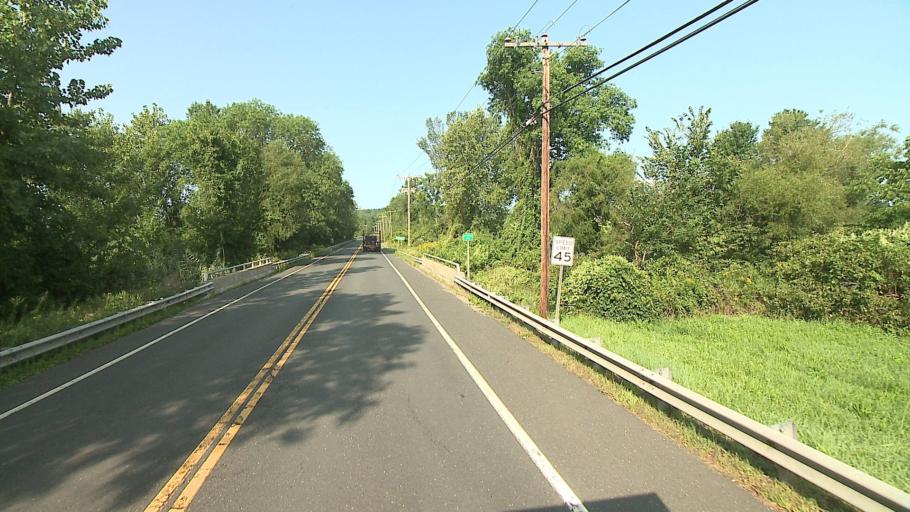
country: US
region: Connecticut
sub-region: Litchfield County
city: Canaan
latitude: 41.9615
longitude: -73.3384
